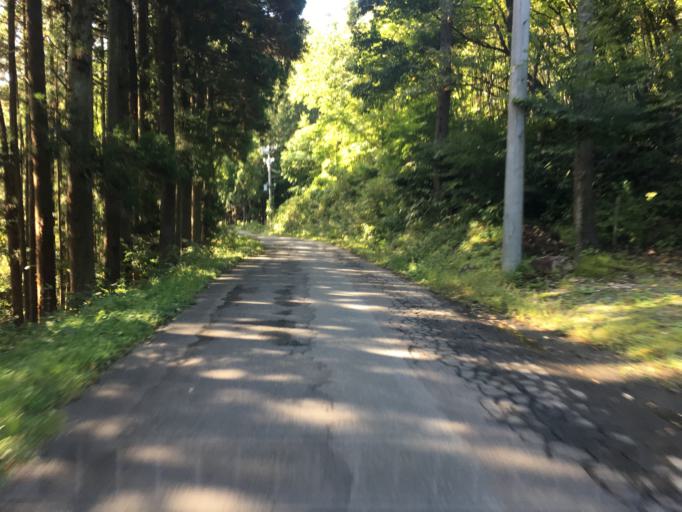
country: JP
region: Yamagata
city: Yonezawa
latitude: 37.8484
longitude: 140.1879
